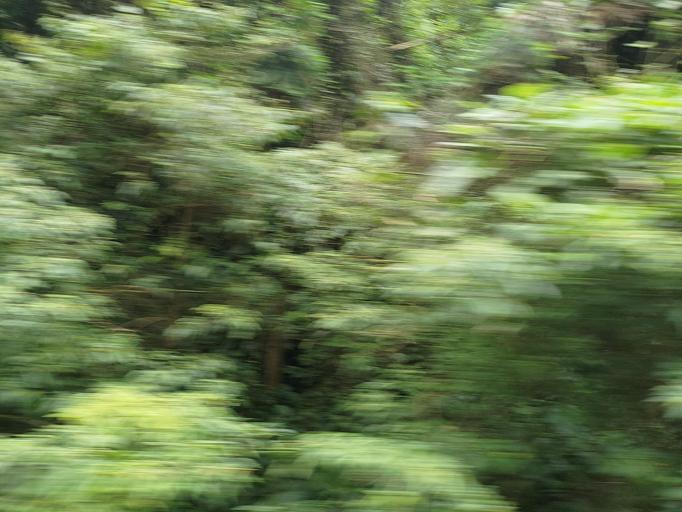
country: TW
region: Taiwan
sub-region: Hsinchu
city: Hsinchu
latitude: 24.6299
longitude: 121.0769
